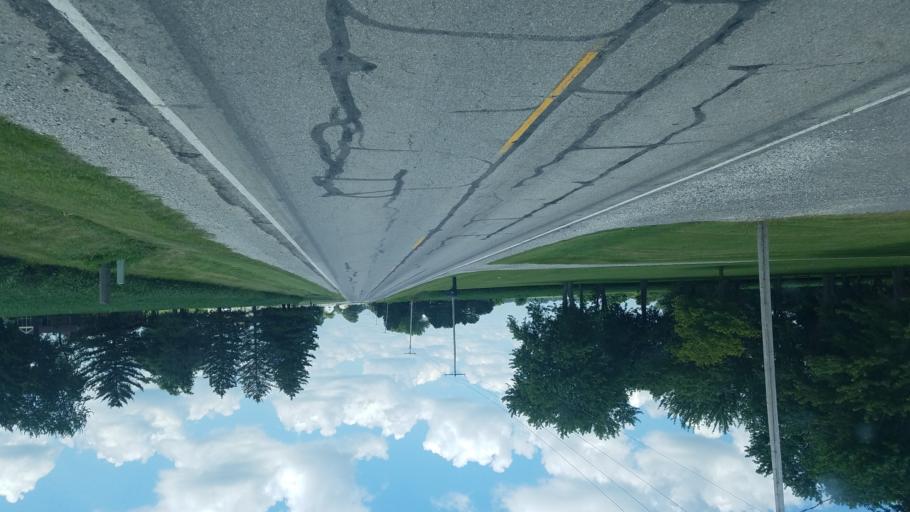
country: US
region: Ohio
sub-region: Marion County
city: Marion
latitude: 40.6303
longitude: -83.0343
